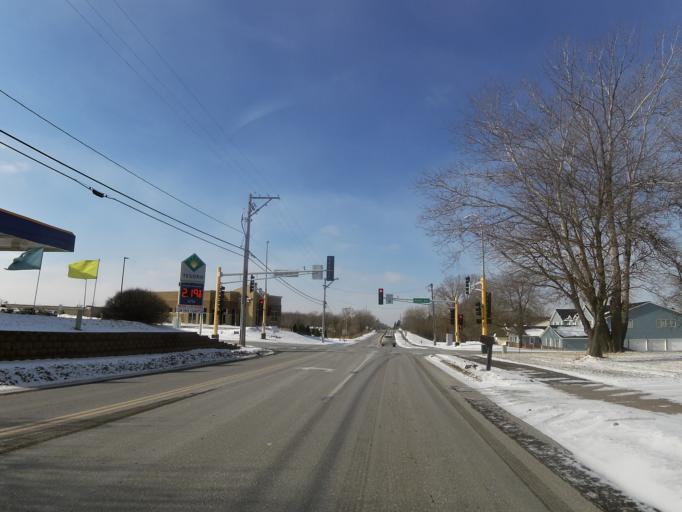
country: US
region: Minnesota
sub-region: Washington County
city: Oakdale
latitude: 44.9704
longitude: -92.9546
